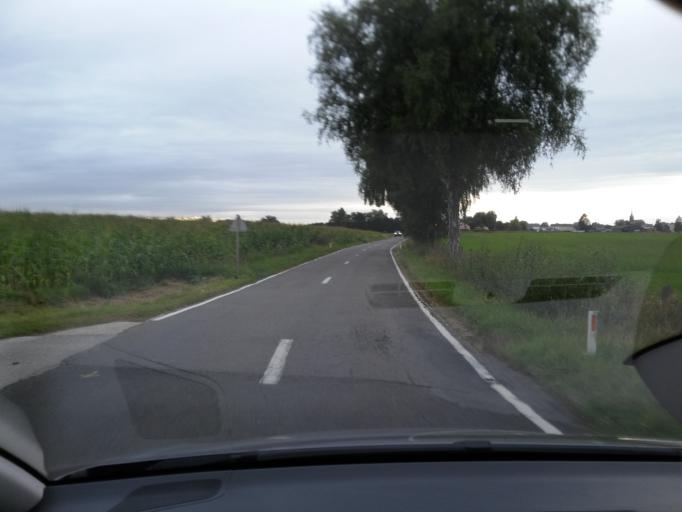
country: BE
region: Wallonia
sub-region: Province du Luxembourg
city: Etalle
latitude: 49.6713
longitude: 5.5776
